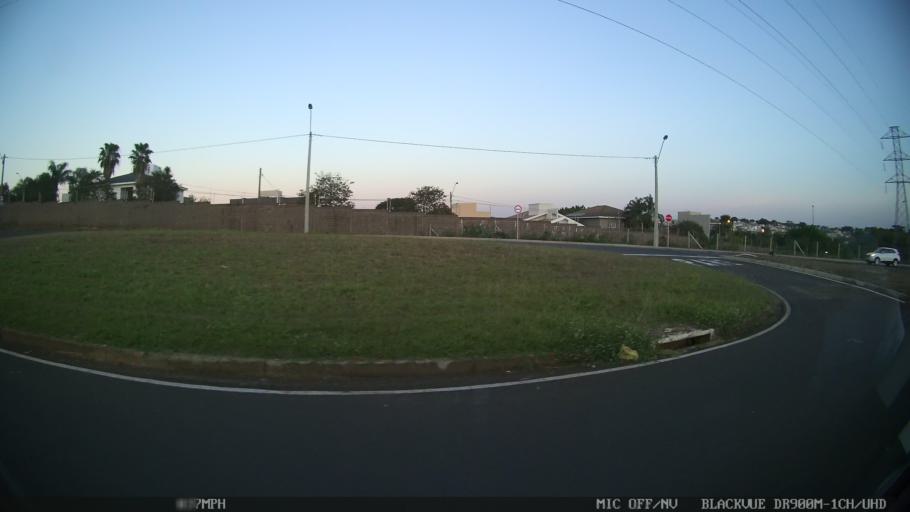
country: BR
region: Sao Paulo
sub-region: Sao Jose Do Rio Preto
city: Sao Jose do Rio Preto
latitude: -20.8246
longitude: -49.3423
